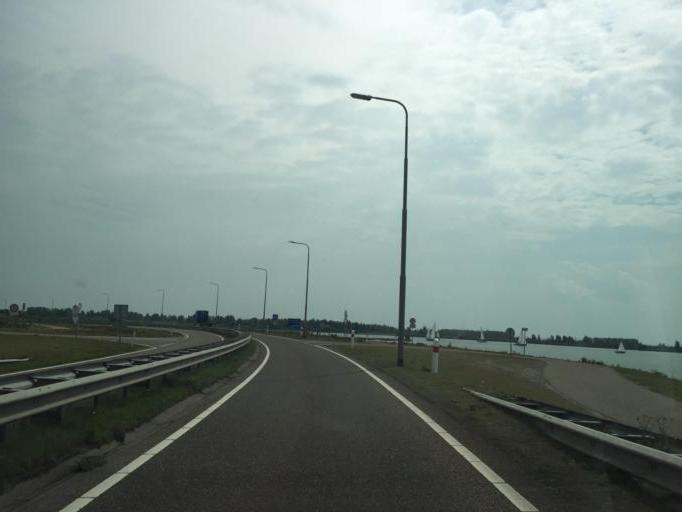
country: NL
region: North Holland
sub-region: Gemeente Enkhuizen
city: Enkhuizen
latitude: 52.6905
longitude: 5.2865
